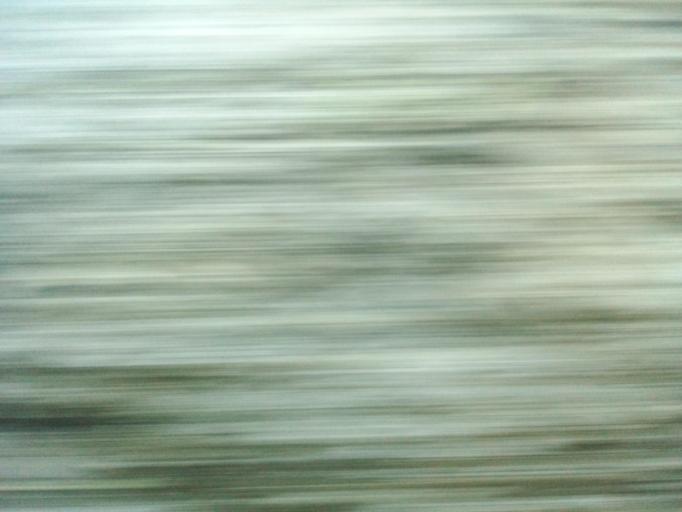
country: BR
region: Minas Gerais
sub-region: Rio Piracicaba
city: Rio Piracicaba
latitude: -19.9524
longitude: -43.1953
